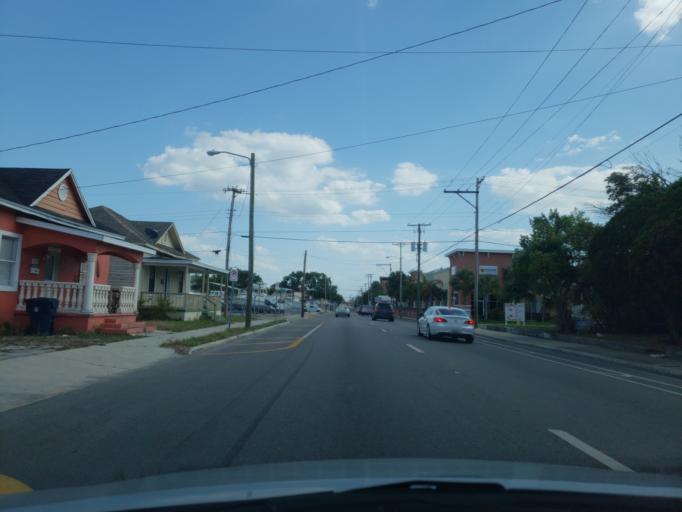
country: US
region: Florida
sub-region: Hillsborough County
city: Tampa
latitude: 27.9701
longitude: -82.4848
